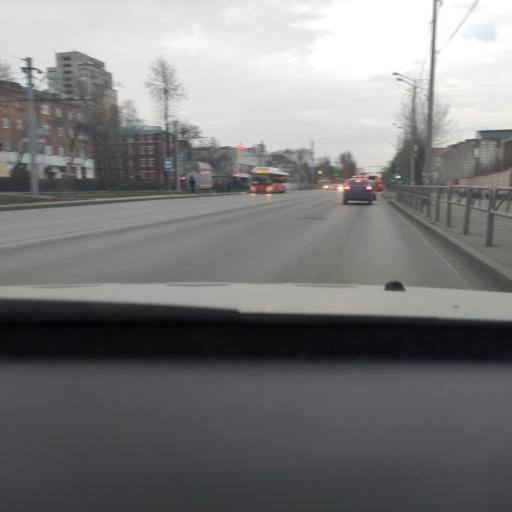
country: RU
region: Perm
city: Perm
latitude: 58.0284
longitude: 56.2963
